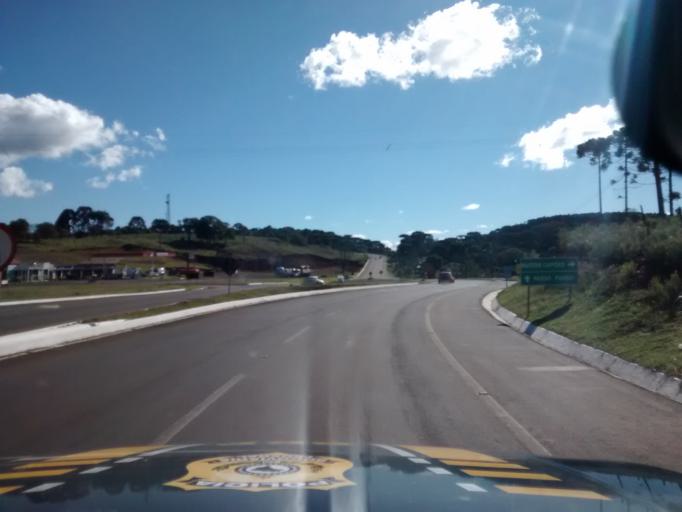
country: BR
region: Rio Grande do Sul
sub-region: Vacaria
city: Vacaria
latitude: -28.3254
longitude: -51.1875
